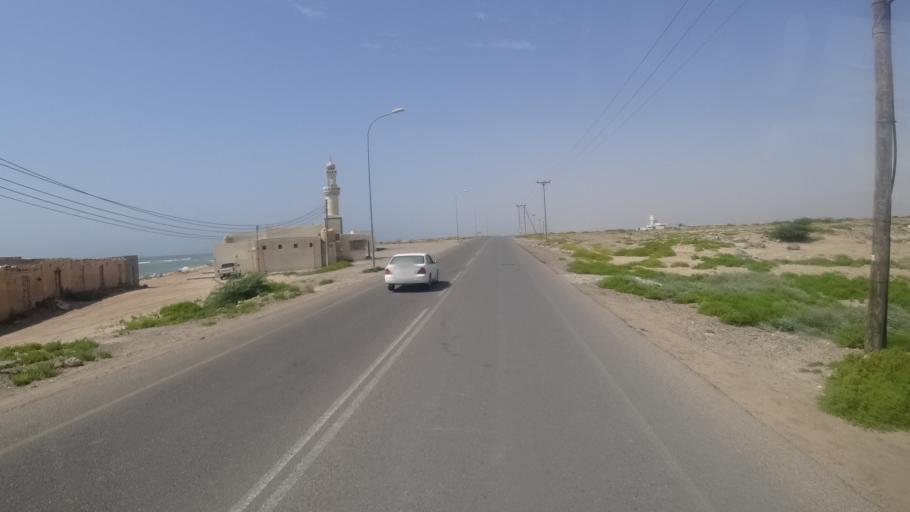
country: OM
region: Ash Sharqiyah
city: Sur
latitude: 22.1119
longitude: 59.7106
